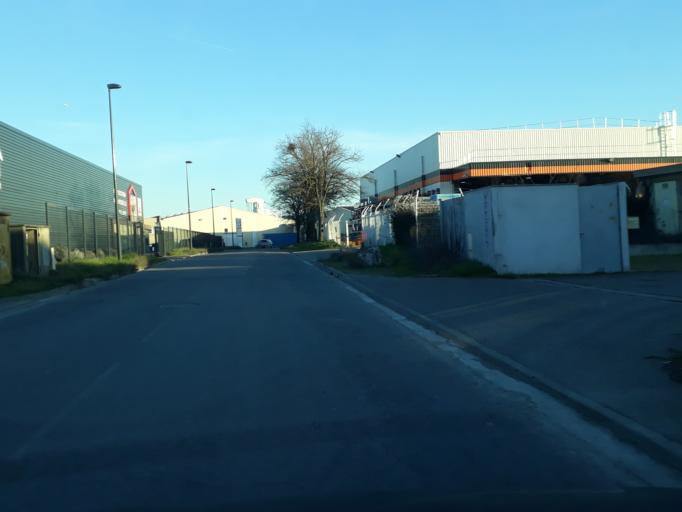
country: FR
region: Midi-Pyrenees
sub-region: Departement de la Haute-Garonne
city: Portet-sur-Garonne
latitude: 43.5527
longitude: 1.4167
